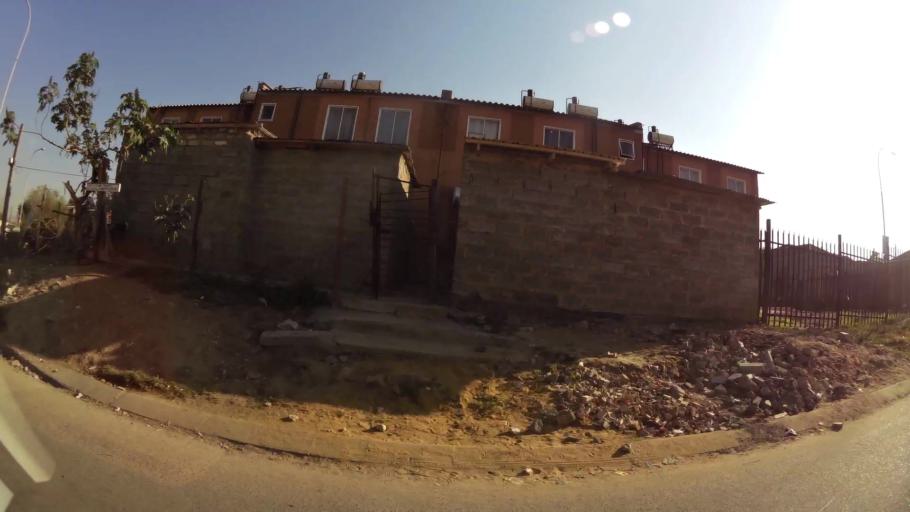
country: ZA
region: Gauteng
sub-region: City of Johannesburg Metropolitan Municipality
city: Modderfontein
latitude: -26.0989
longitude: 28.1170
